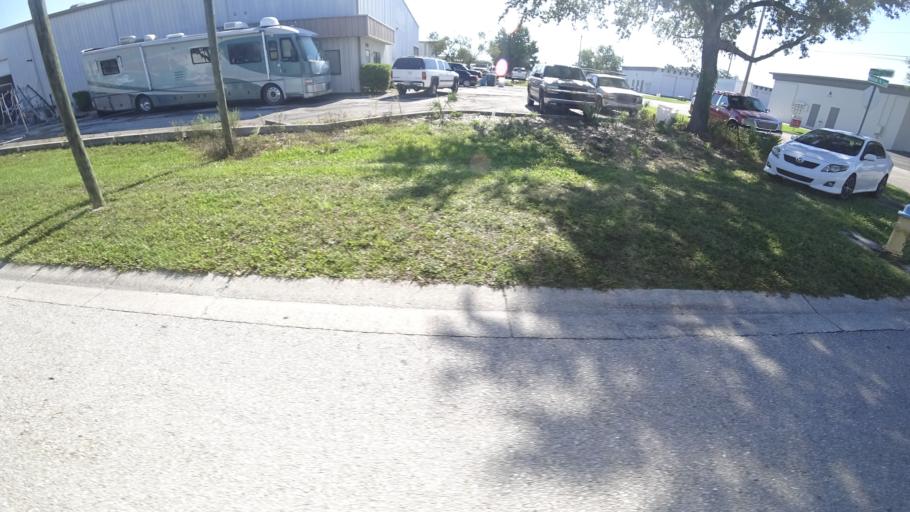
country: US
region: Florida
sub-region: Manatee County
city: Whitfield
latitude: 27.4191
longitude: -82.5400
